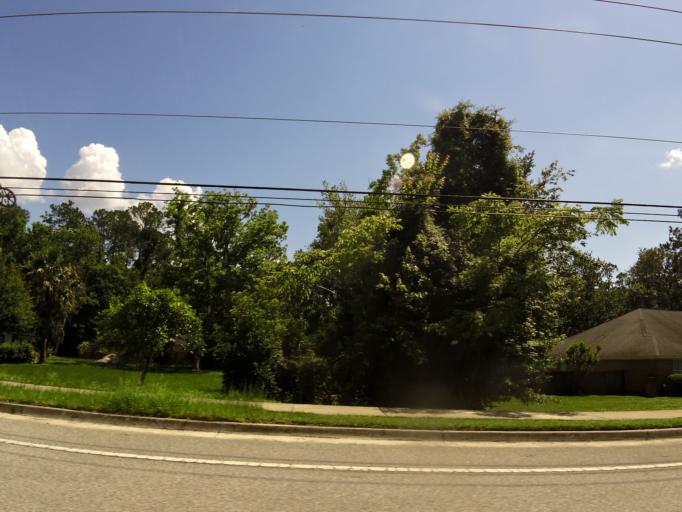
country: US
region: Florida
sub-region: Saint Johns County
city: Fruit Cove
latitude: 30.1560
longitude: -81.5927
